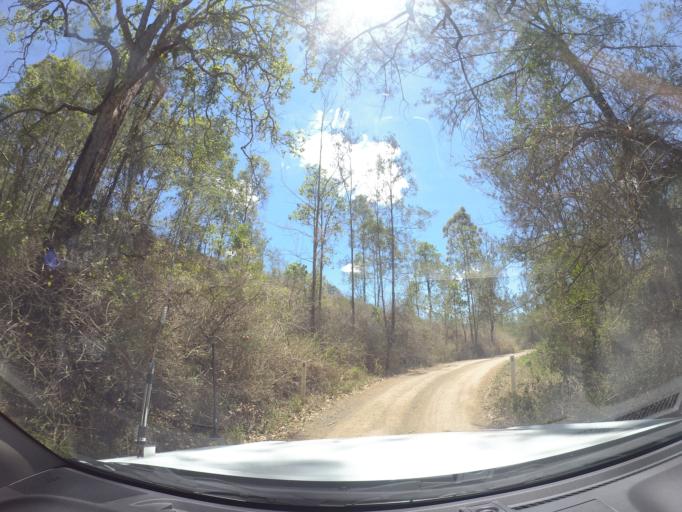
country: AU
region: Queensland
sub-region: Ipswich
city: Springfield Lakes
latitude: -27.8192
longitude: 152.8462
